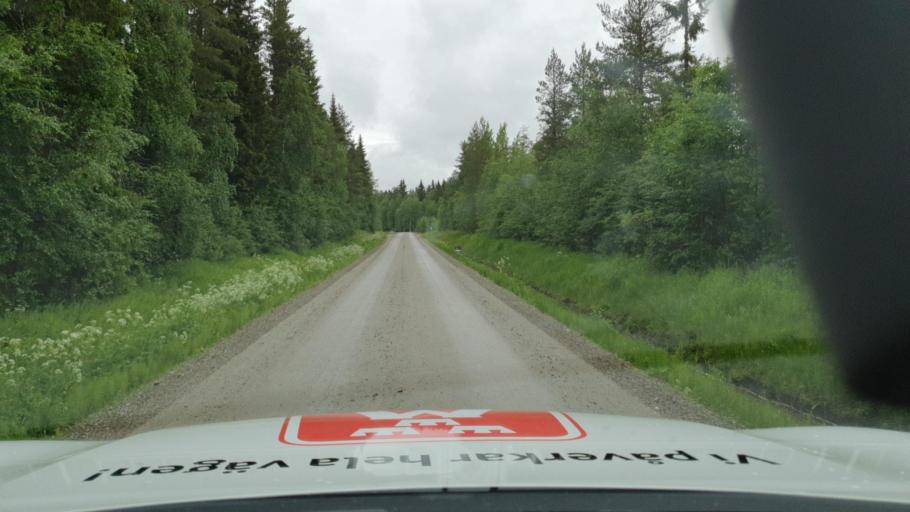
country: SE
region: Vaesterbotten
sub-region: Dorotea Kommun
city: Dorotea
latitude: 64.0095
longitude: 16.7984
